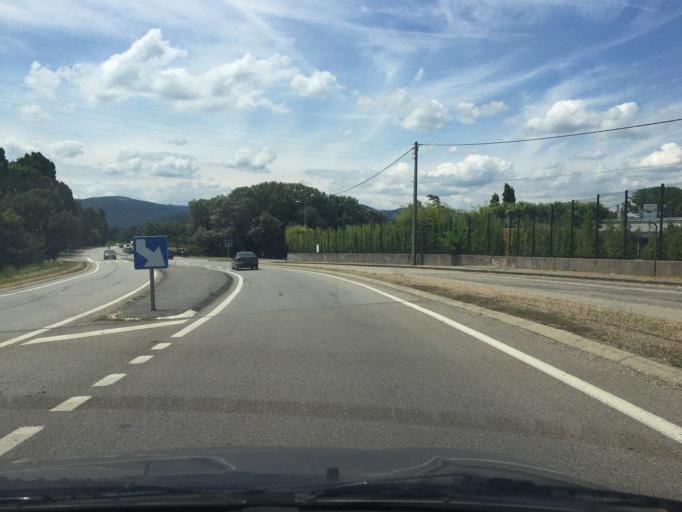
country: FR
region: Rhone-Alpes
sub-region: Departement de l'Ardeche
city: Charmes-sur-Rhone
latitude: 44.8447
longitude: 4.8625
